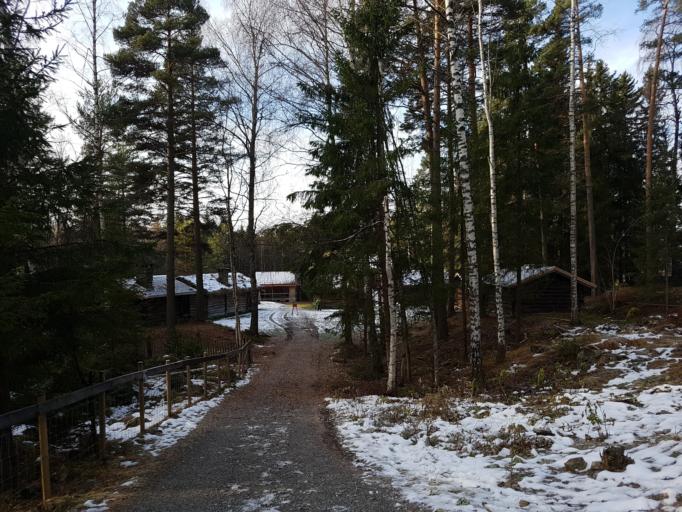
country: NO
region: Oppland
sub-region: Lillehammer
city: Lillehammer
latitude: 61.1119
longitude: 10.4832
